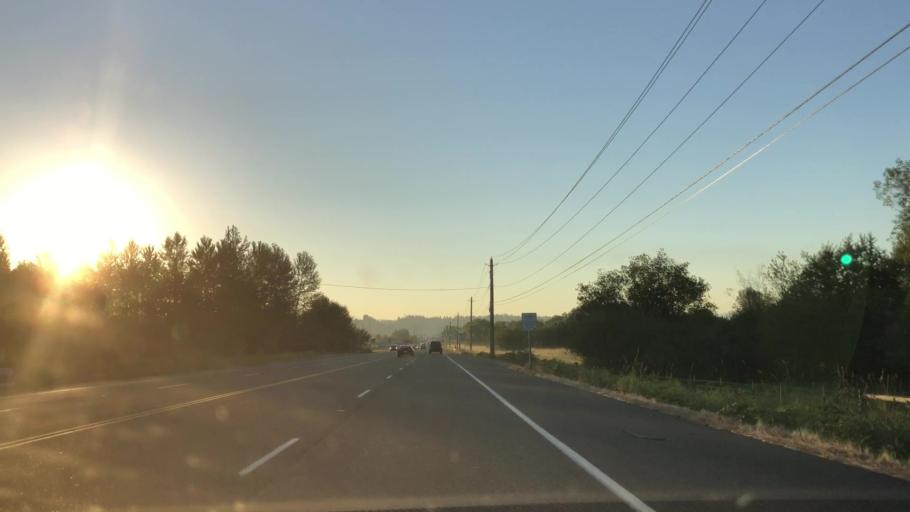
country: US
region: Washington
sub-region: King County
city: Lakeland North
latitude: 47.3536
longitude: -122.2608
